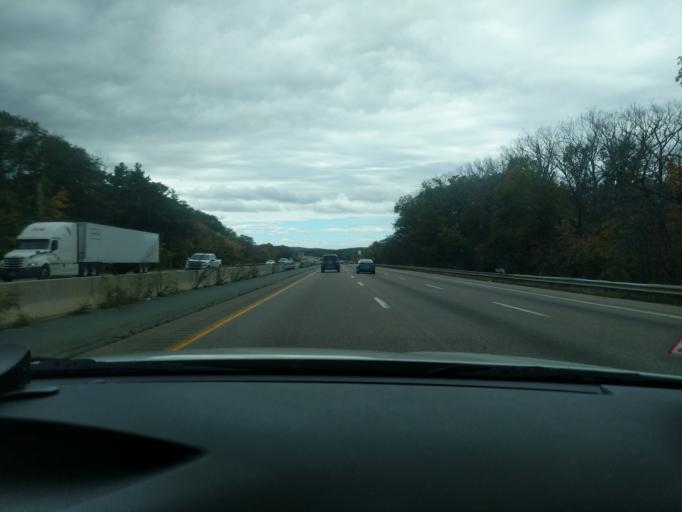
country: US
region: Massachusetts
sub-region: Worcester County
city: Cordaville
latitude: 42.2722
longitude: -71.5490
